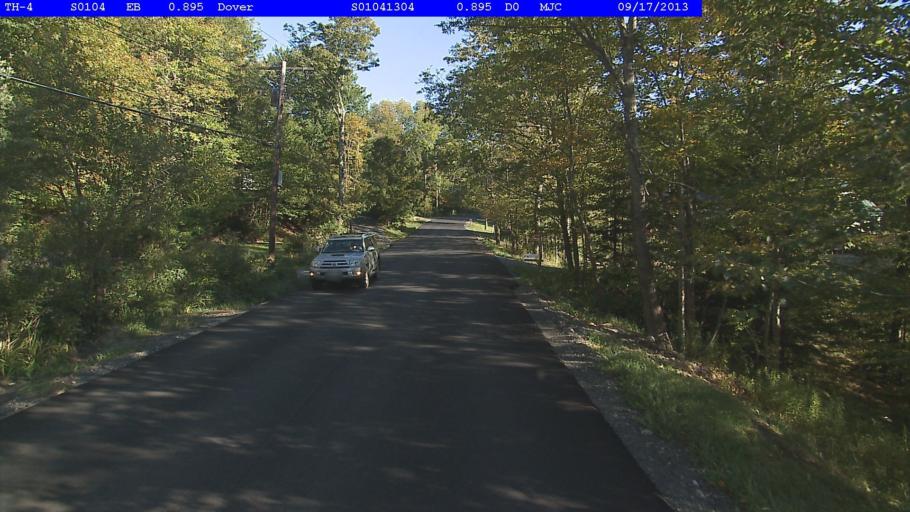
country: US
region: Vermont
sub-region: Windham County
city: Dover
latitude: 42.9282
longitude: -72.8395
